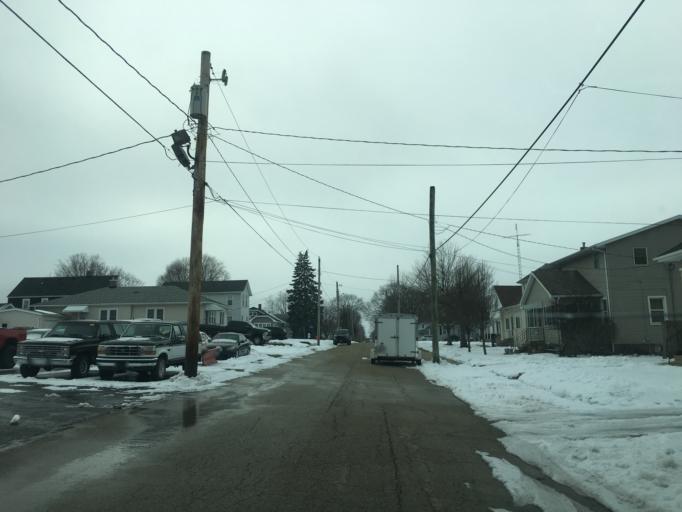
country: US
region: Illinois
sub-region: LaSalle County
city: Peru
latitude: 41.3339
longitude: -89.1293
